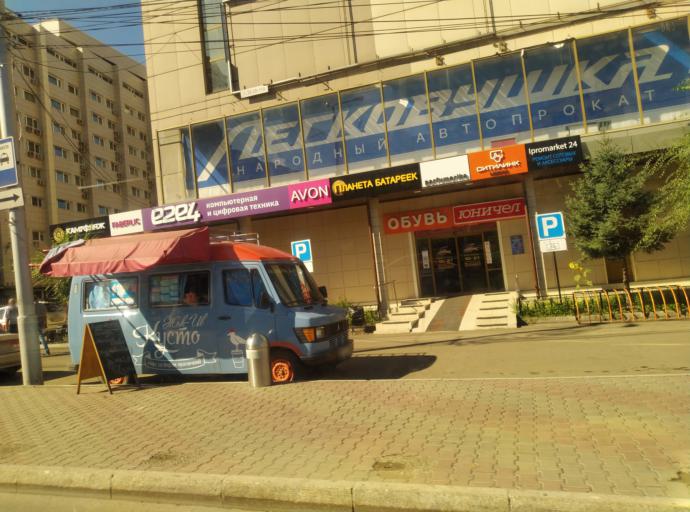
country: RU
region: Krasnoyarskiy
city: Krasnoyarsk
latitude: 56.0100
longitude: 92.8711
